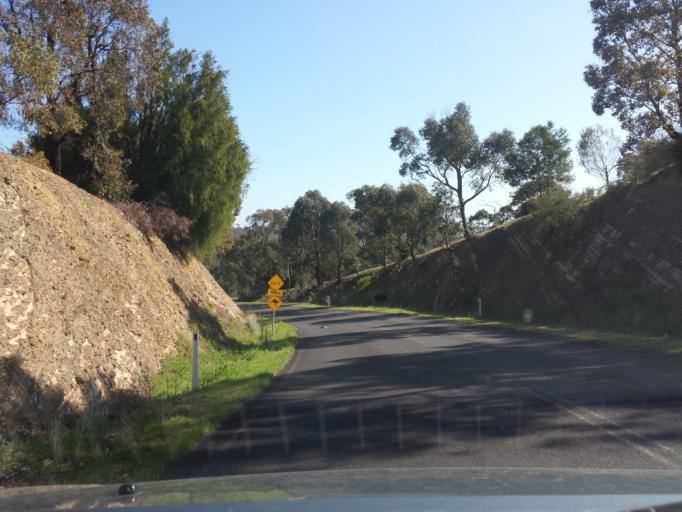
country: AU
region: Victoria
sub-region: Nillumbik
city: Saint Andrews
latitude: -37.6609
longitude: 145.2901
